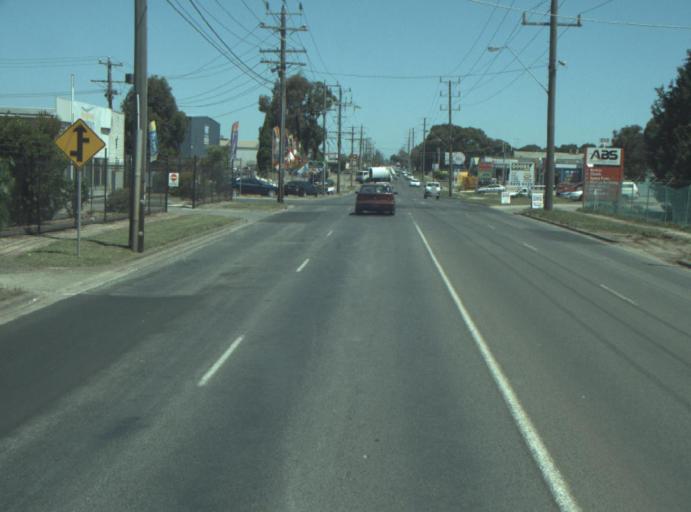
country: AU
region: Victoria
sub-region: Greater Geelong
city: Bell Park
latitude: -38.1064
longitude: 144.3443
